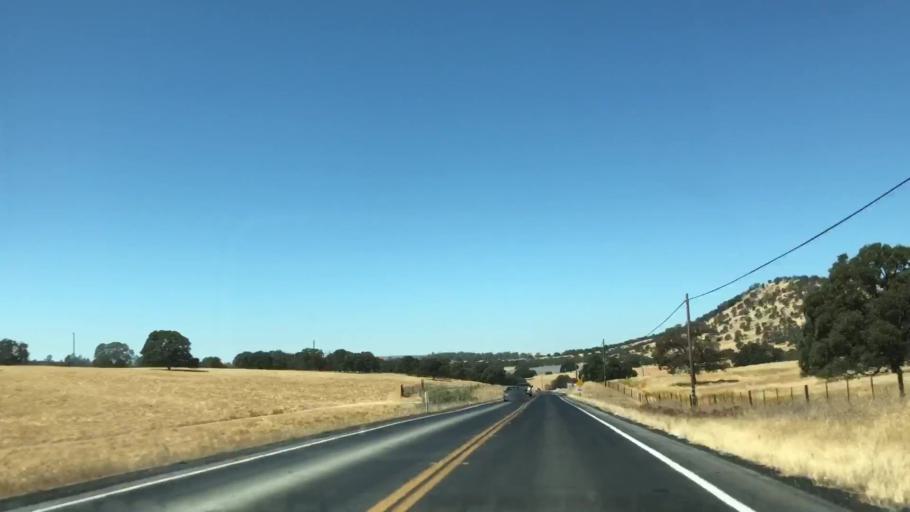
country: US
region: California
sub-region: Tuolumne County
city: Jamestown
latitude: 37.8867
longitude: -120.5126
